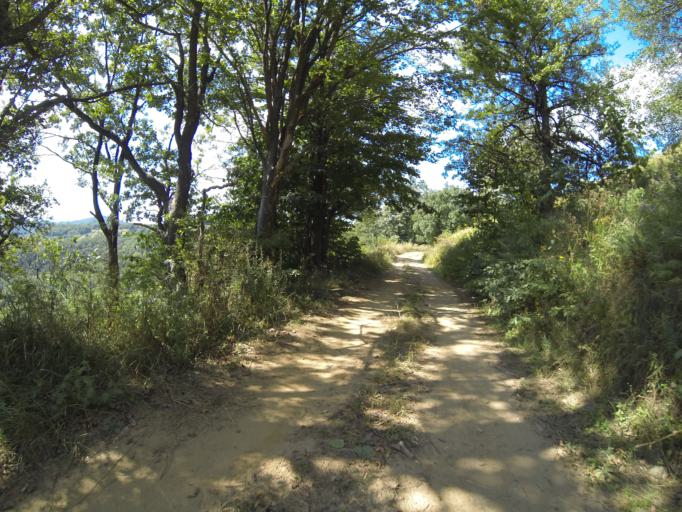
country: RO
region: Mehedinti
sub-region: Comuna Svinita
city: Svinita
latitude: 44.5604
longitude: 22.1356
